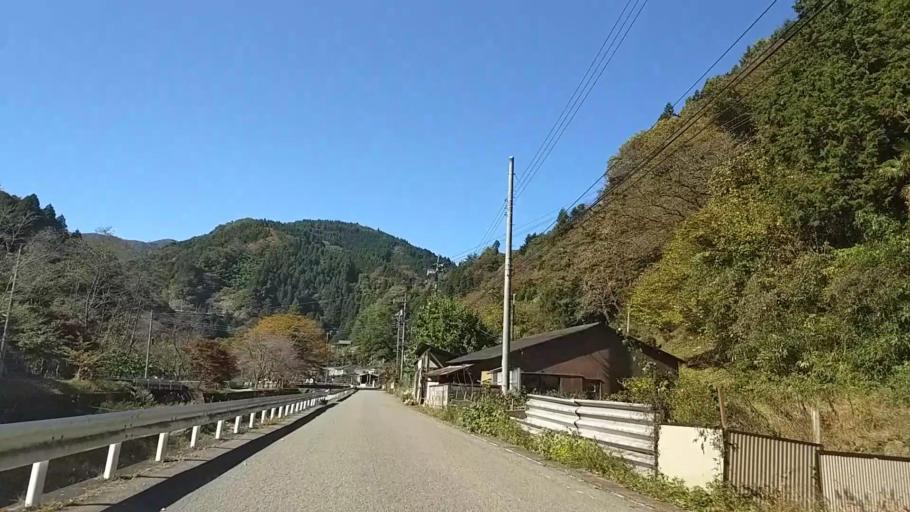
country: JP
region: Yamanashi
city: Otsuki
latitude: 35.7074
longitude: 139.0085
